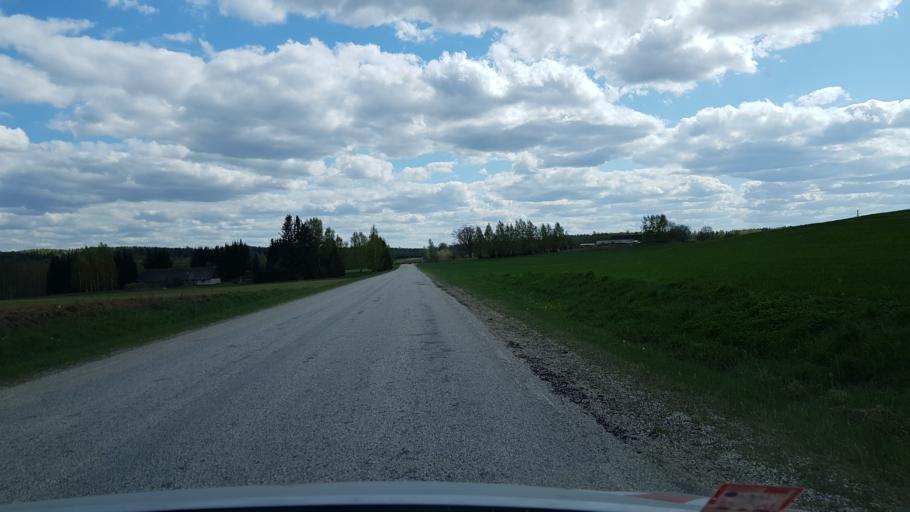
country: EE
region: Tartu
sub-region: UElenurme vald
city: Ulenurme
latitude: 58.2731
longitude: 26.9072
